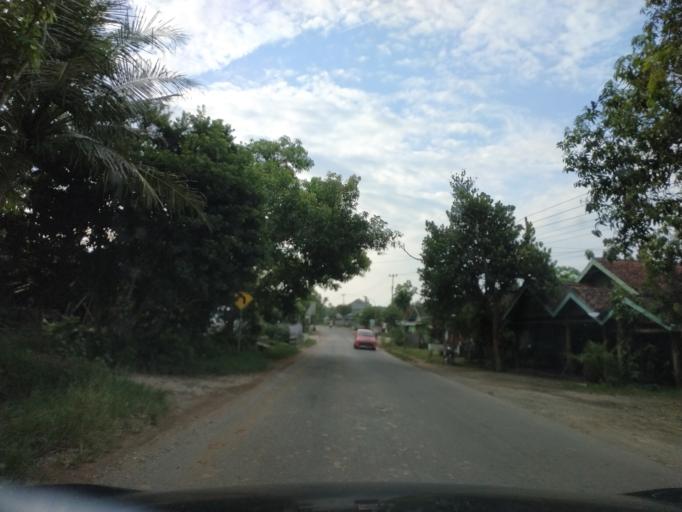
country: ID
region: Central Java
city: Ngampel
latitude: -6.8943
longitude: 111.4397
